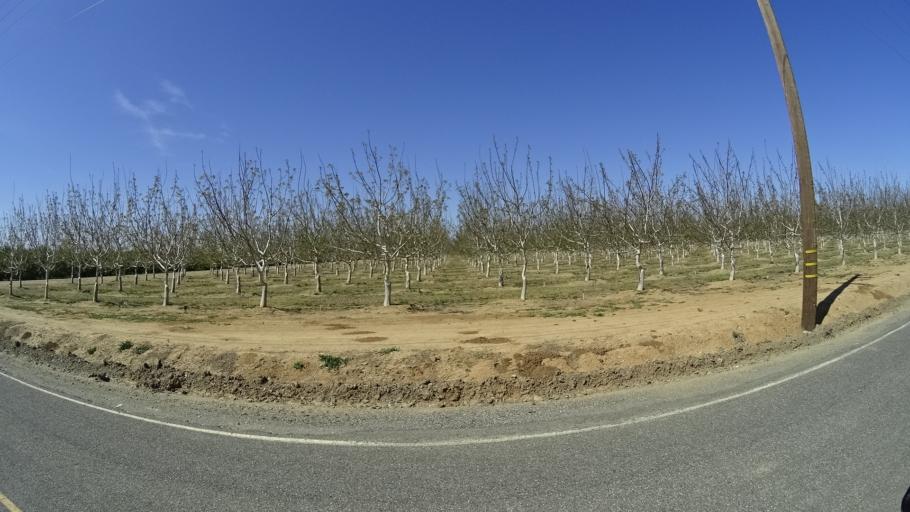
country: US
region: California
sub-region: Glenn County
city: Orland
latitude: 39.7044
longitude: -122.1782
